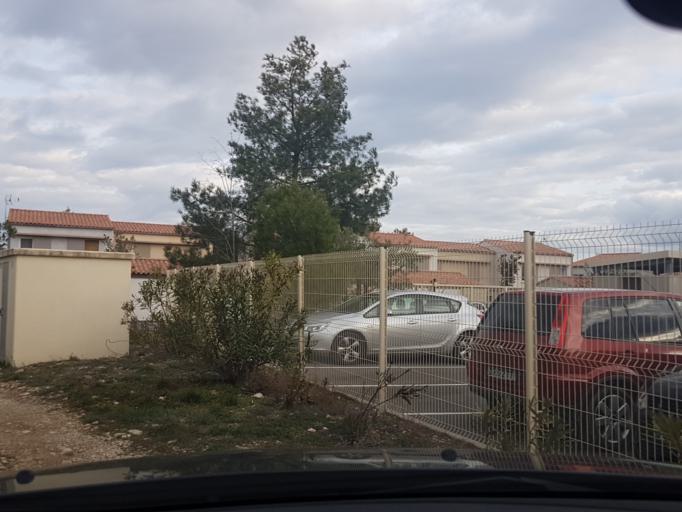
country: FR
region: Provence-Alpes-Cote d'Azur
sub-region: Departement des Bouches-du-Rhone
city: Eygalieres
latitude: 43.7536
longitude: 4.9517
